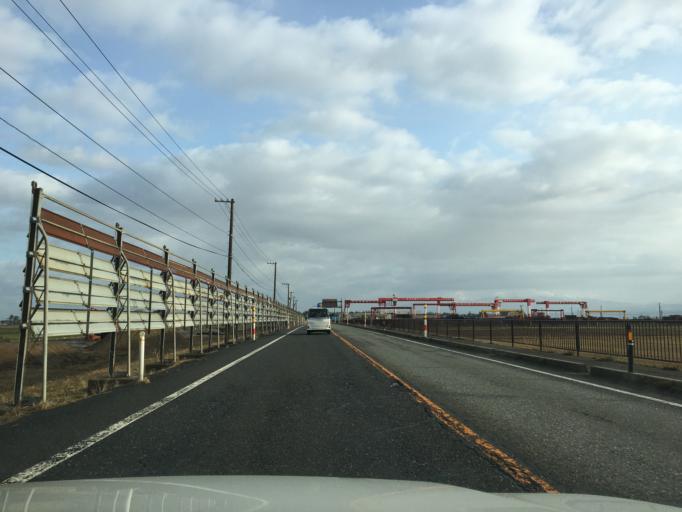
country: JP
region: Yamagata
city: Sakata
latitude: 38.8367
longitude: 139.8482
